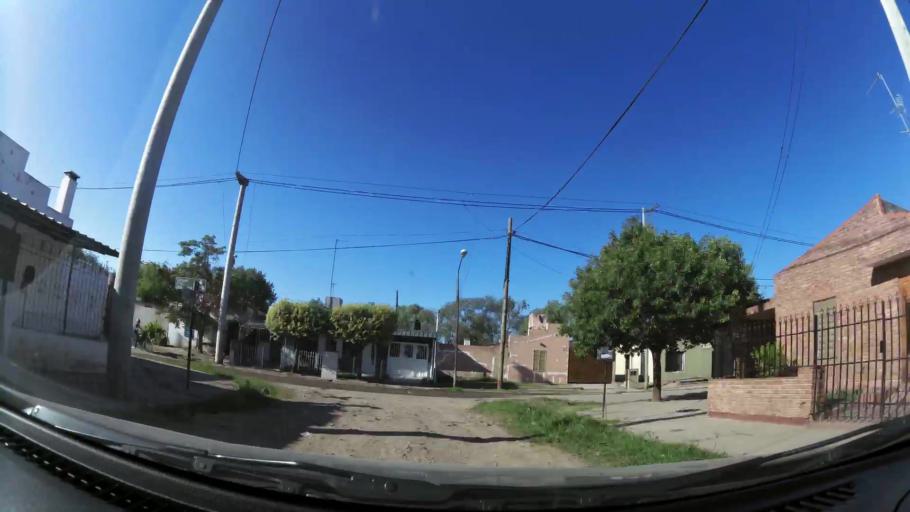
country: AR
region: Cordoba
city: Villa Allende
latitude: -31.3372
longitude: -64.2471
